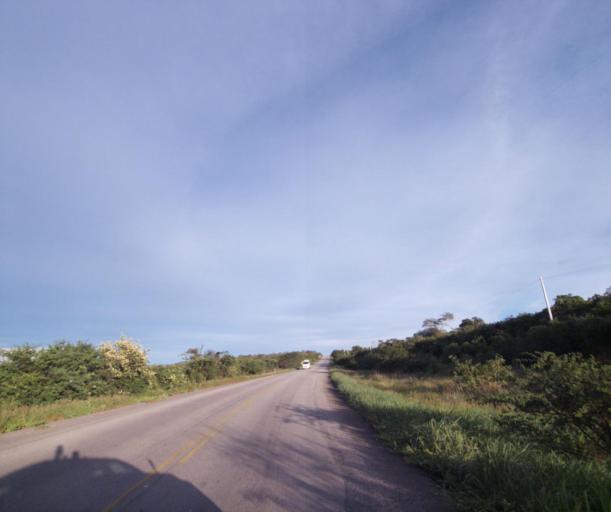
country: BR
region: Bahia
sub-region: Cacule
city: Cacule
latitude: -14.2030
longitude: -42.0584
